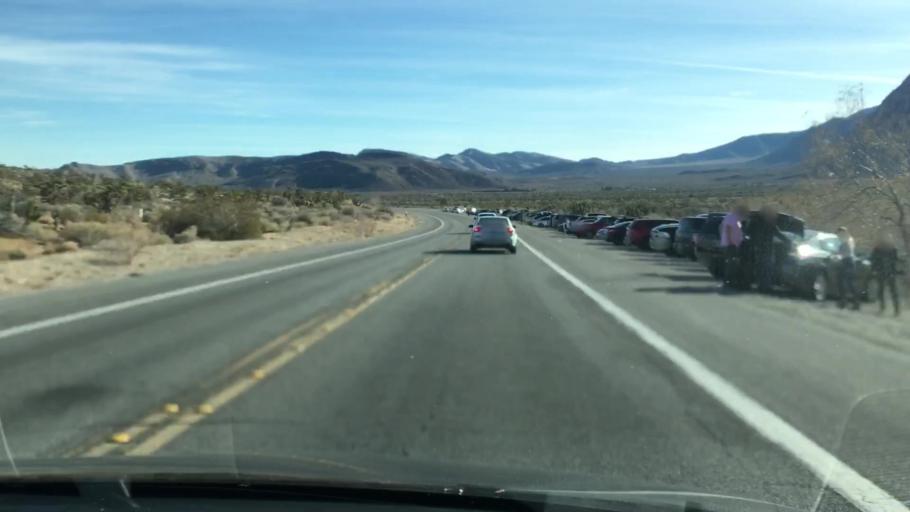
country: US
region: Nevada
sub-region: Clark County
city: Summerlin South
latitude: 36.0819
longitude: -115.4479
